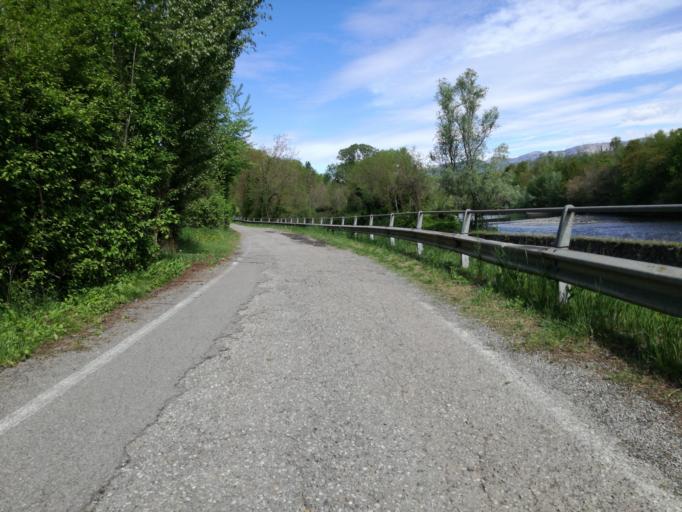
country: IT
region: Lombardy
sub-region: Provincia di Monza e Brianza
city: Porto d'Adda
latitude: 45.6595
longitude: 9.4870
